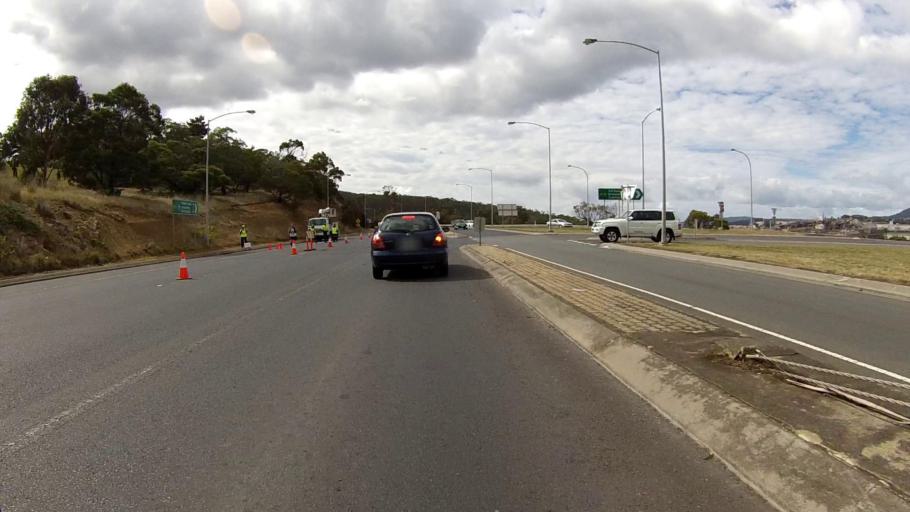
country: AU
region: Tasmania
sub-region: Glenorchy
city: Lutana
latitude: -42.8140
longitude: 147.3149
